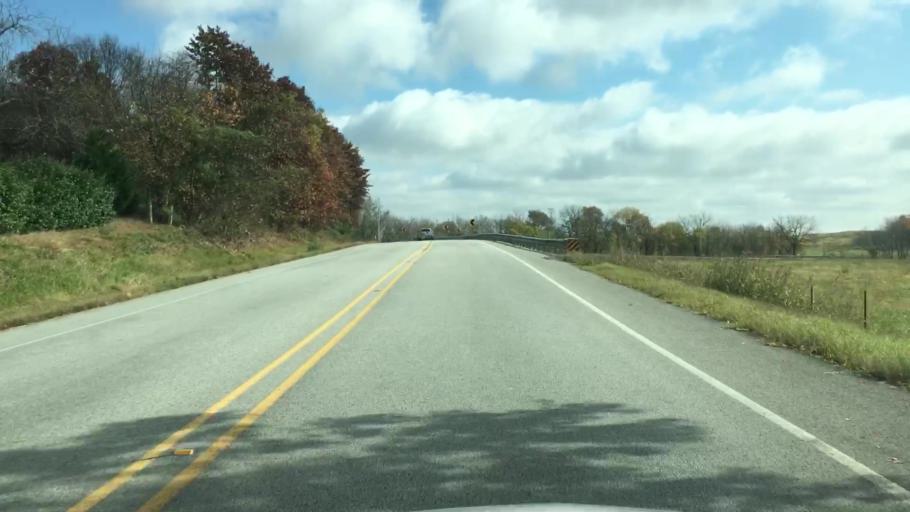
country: US
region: Arkansas
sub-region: Benton County
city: Centerton
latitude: 36.3024
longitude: -94.3242
